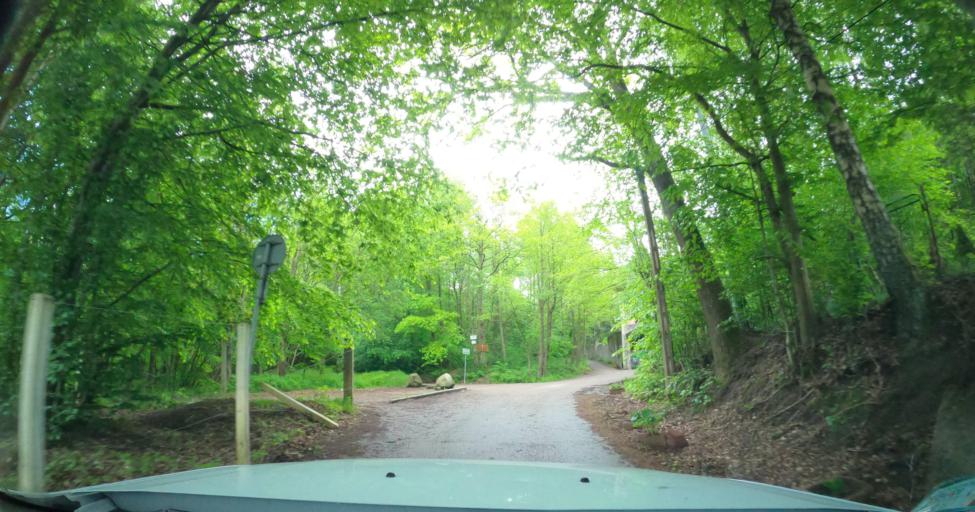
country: PL
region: Pomeranian Voivodeship
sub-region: Powiat kartuski
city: Garcz
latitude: 54.3318
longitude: 18.1406
